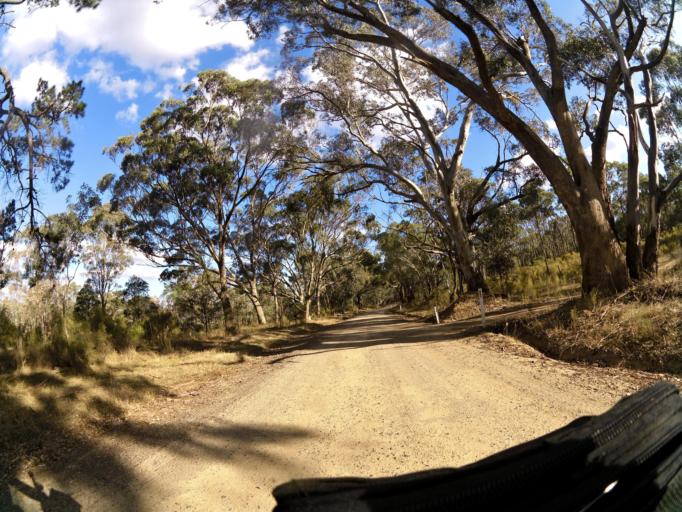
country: AU
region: Victoria
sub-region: Greater Bendigo
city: Kennington
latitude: -37.0105
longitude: 144.8094
